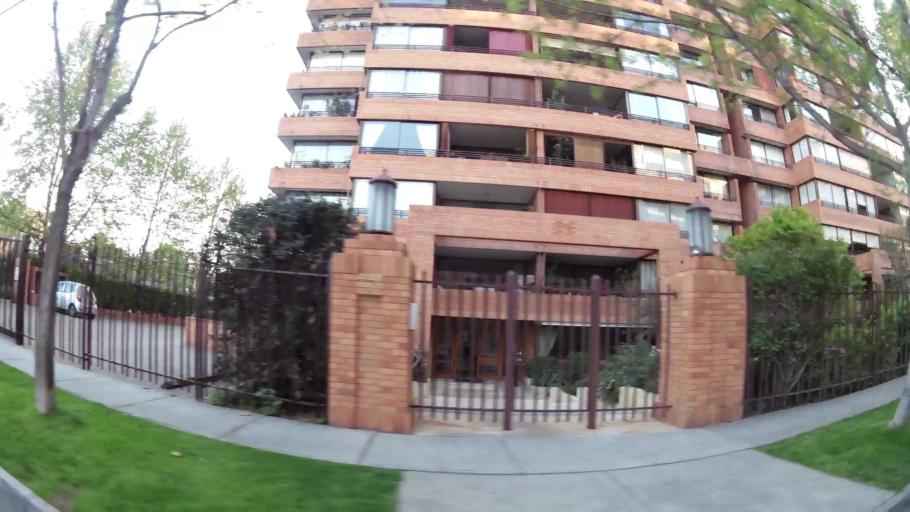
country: CL
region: Santiago Metropolitan
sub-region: Provincia de Santiago
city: Villa Presidente Frei, Nunoa, Santiago, Chile
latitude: -33.3978
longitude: -70.5644
